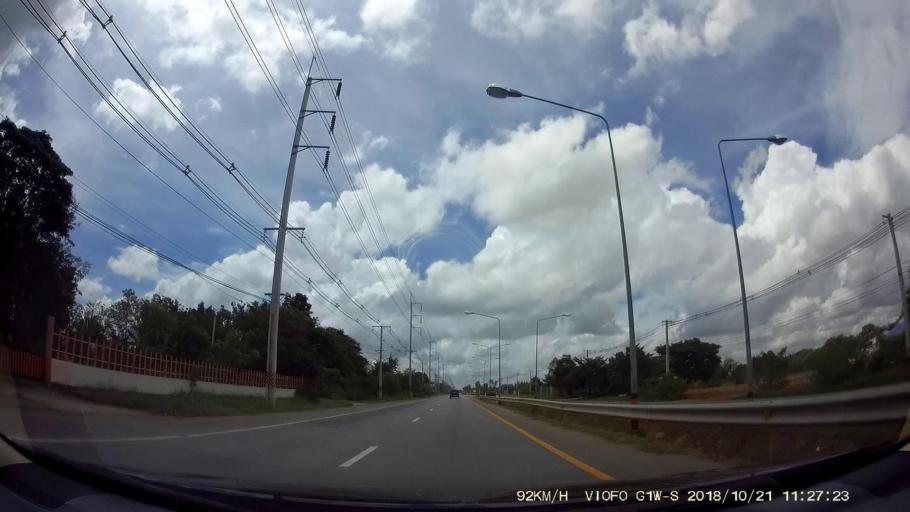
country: TH
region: Chaiyaphum
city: Chaiyaphum
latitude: 15.8007
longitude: 102.0573
